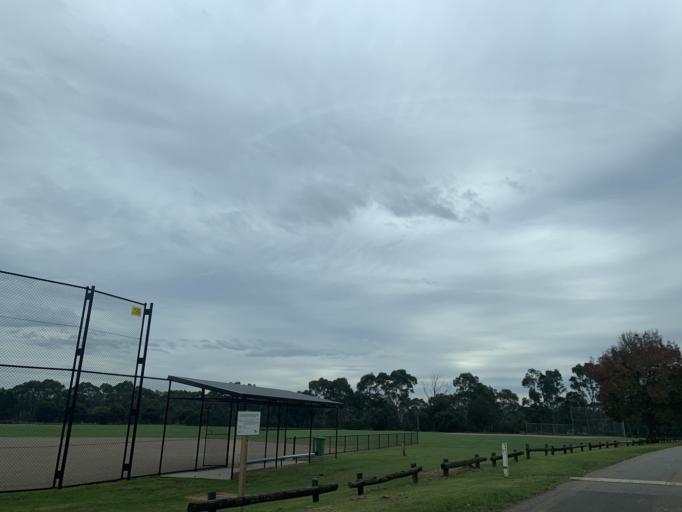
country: AU
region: Victoria
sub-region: Knox
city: Rowville
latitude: -37.9578
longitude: 145.2387
